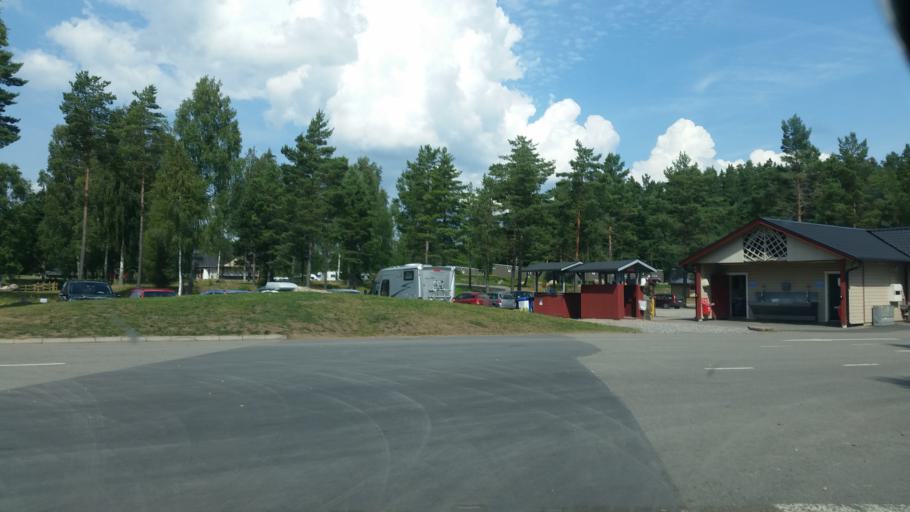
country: SE
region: Vaestra Goetaland
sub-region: Skara Kommun
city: Axvall
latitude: 58.4112
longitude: 13.5554
